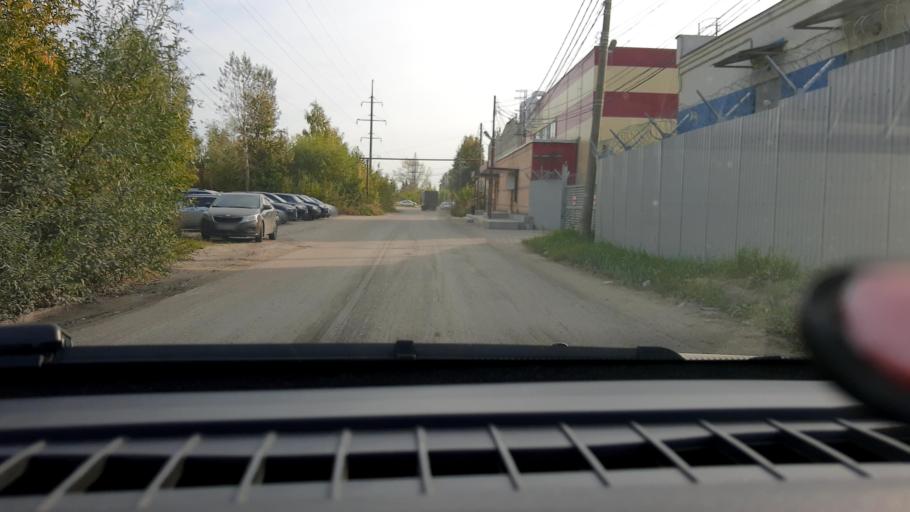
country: RU
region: Nizjnij Novgorod
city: Burevestnik
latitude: 56.1641
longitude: 43.9069
